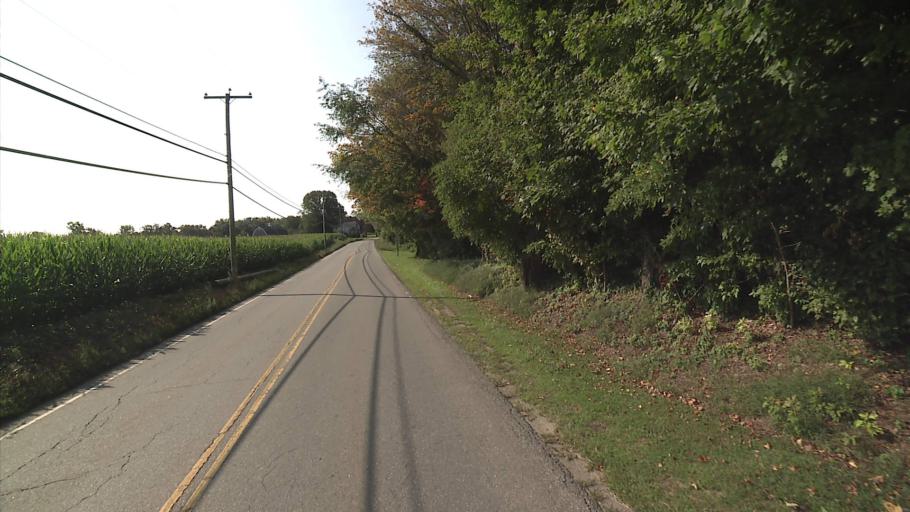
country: US
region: Connecticut
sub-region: Windham County
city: South Windham
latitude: 41.6244
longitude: -72.1975
